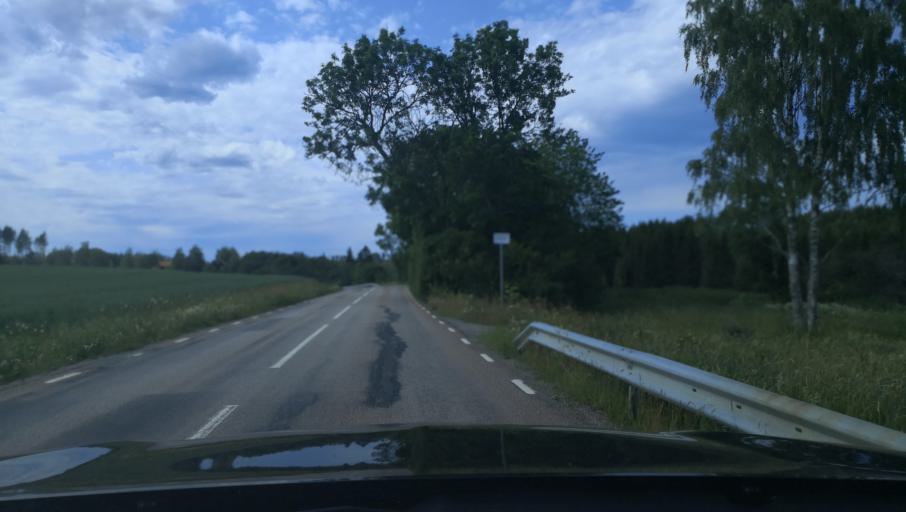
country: SE
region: Dalarna
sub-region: Avesta Kommun
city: Avesta
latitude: 59.9907
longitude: 16.1136
